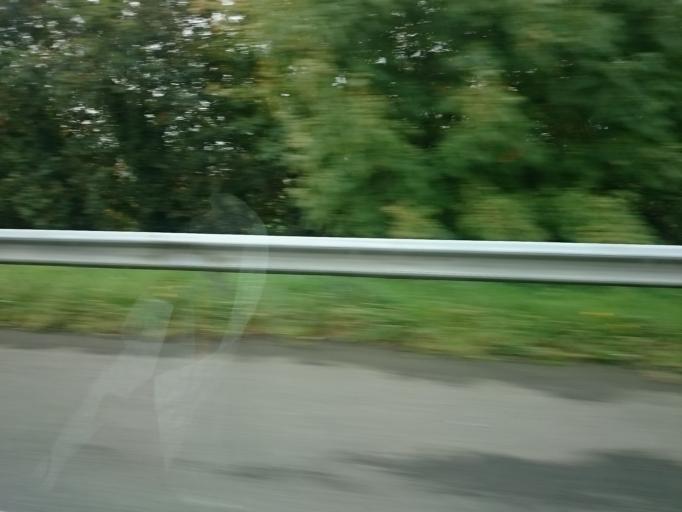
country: FR
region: Brittany
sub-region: Departement du Finistere
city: Guerlesquin
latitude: 48.5721
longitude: -3.6289
